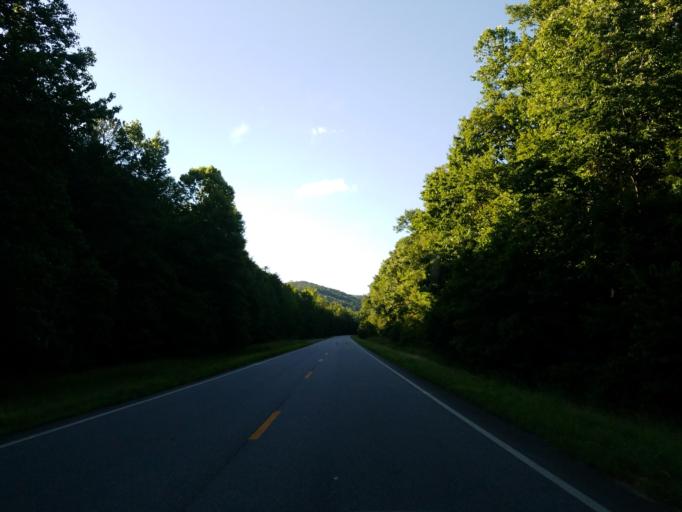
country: US
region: Georgia
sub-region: Whitfield County
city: Dalton
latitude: 34.6369
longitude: -85.0596
